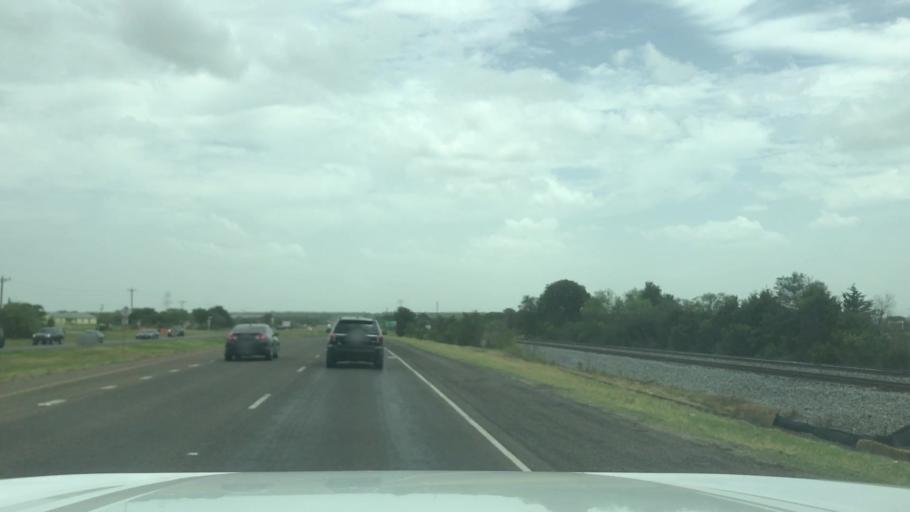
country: US
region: Texas
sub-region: McLennan County
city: Riesel
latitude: 31.5126
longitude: -96.9548
